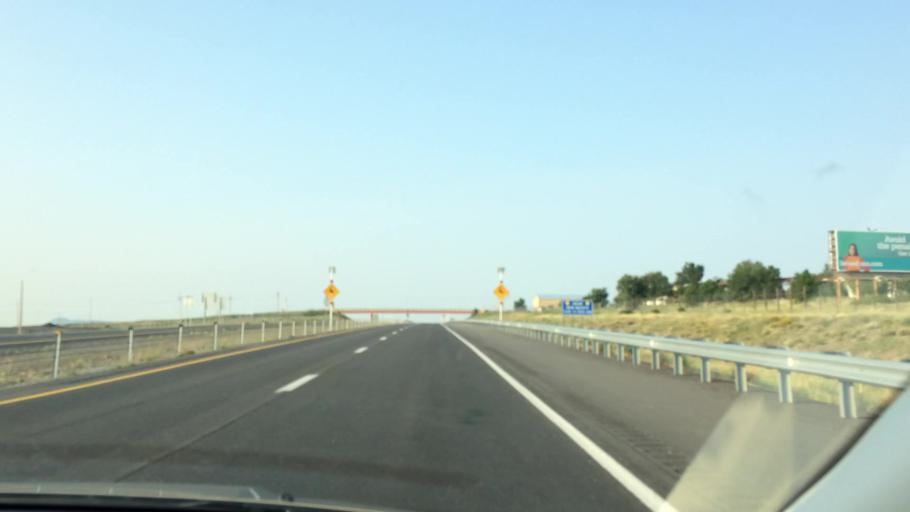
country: US
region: New Mexico
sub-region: Colfax County
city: Raton
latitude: 36.8739
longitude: -104.4357
